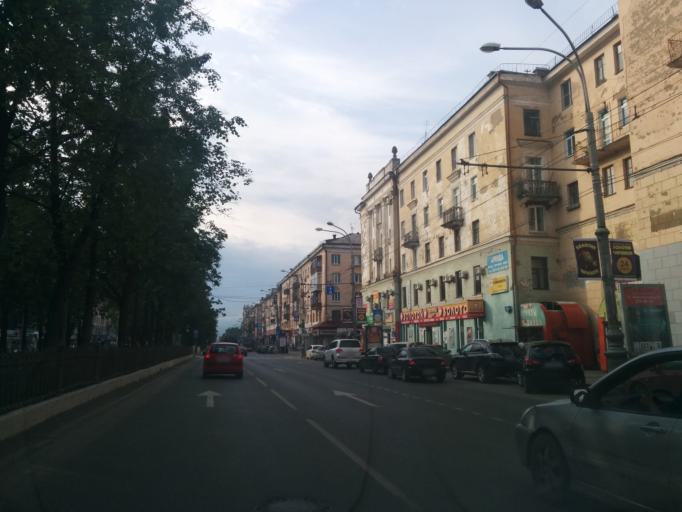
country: RU
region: Perm
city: Perm
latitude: 57.9978
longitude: 56.2519
